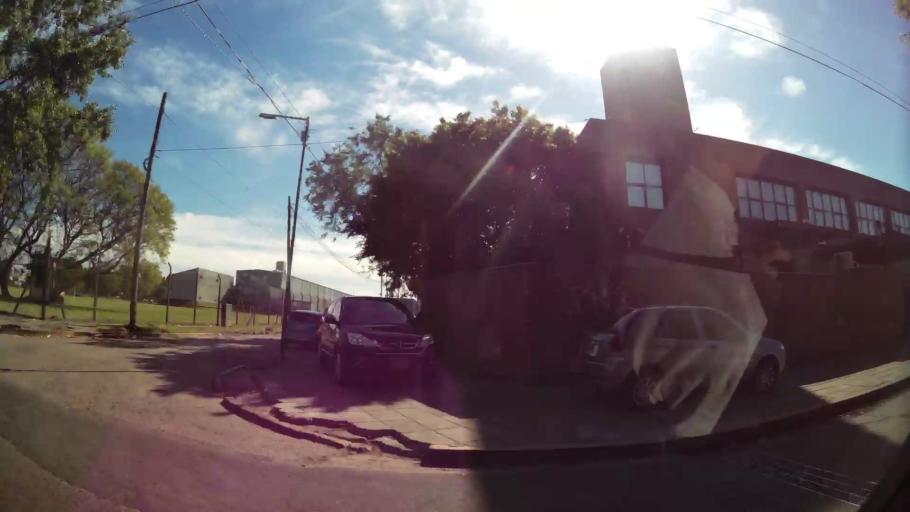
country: AR
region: Buenos Aires
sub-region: Partido de Tigre
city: Tigre
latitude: -34.4742
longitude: -58.5759
